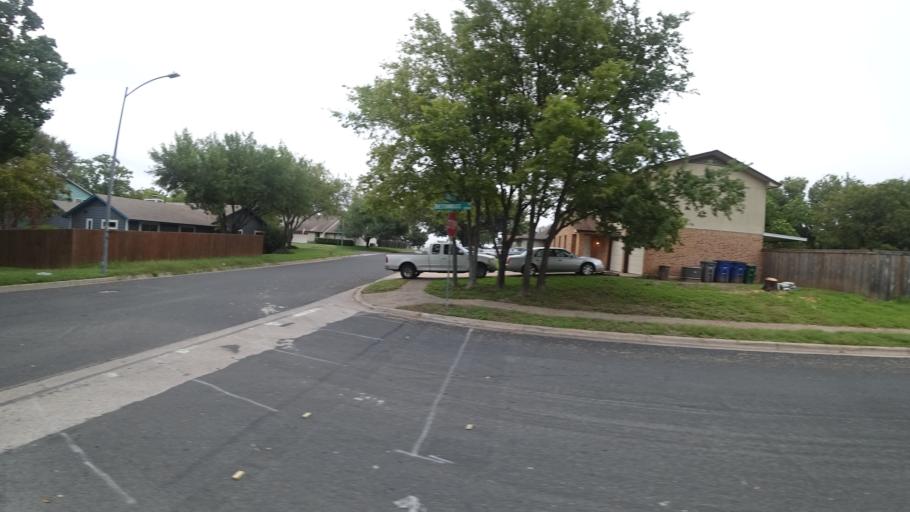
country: US
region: Texas
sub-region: Travis County
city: Austin
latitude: 30.3429
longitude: -97.6912
